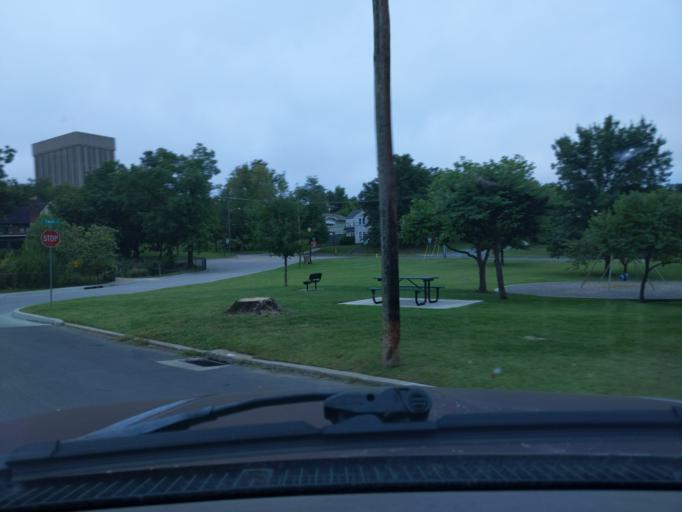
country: US
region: Oklahoma
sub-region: Tulsa County
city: Tulsa
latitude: 36.1358
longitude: -95.9708
